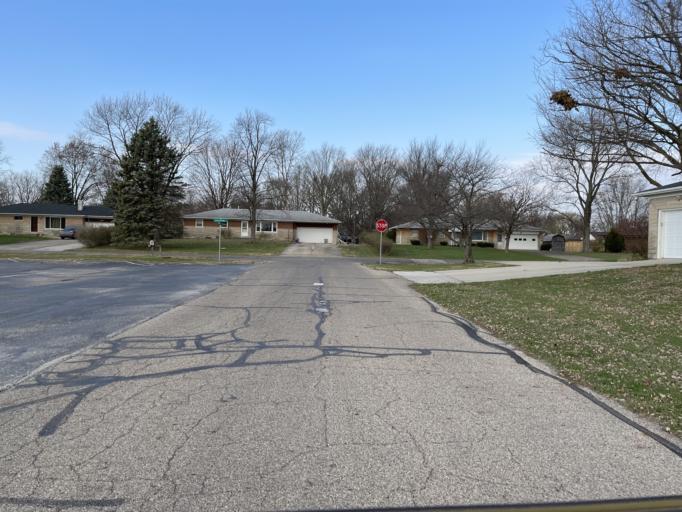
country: US
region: Indiana
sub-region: Hendricks County
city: Avon
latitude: 39.7634
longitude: -86.3966
